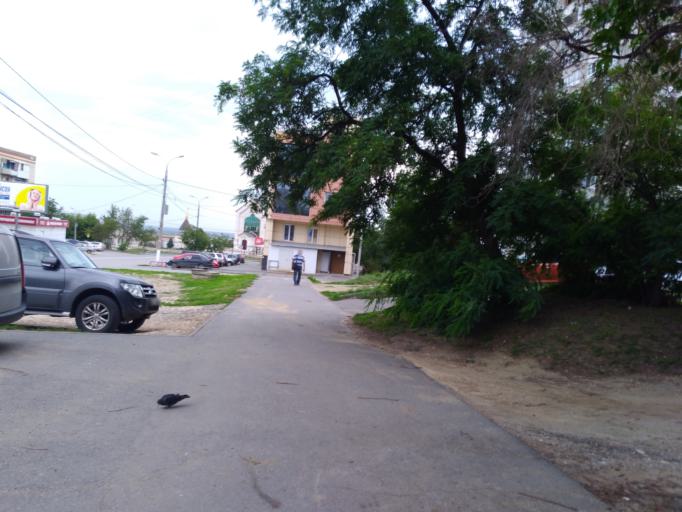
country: RU
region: Volgograd
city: Volgograd
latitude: 48.7198
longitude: 44.5200
